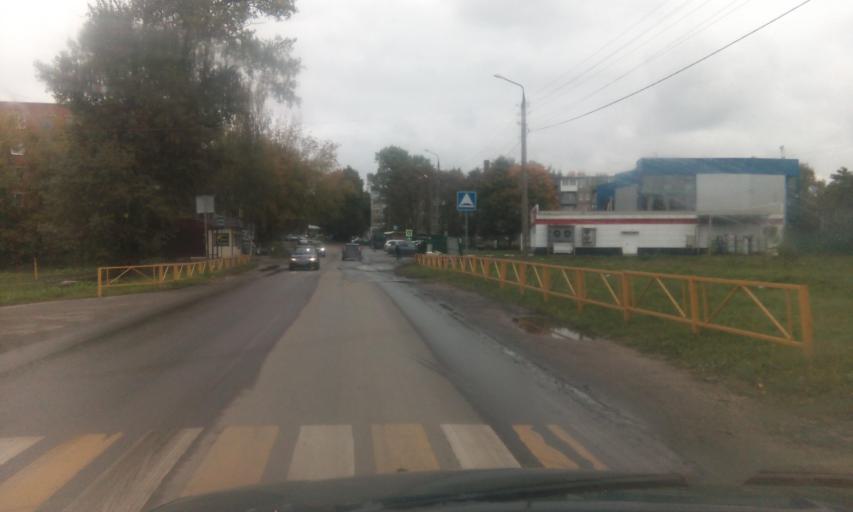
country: RU
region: Tula
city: Uzlovaya
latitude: 53.9745
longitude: 38.1542
